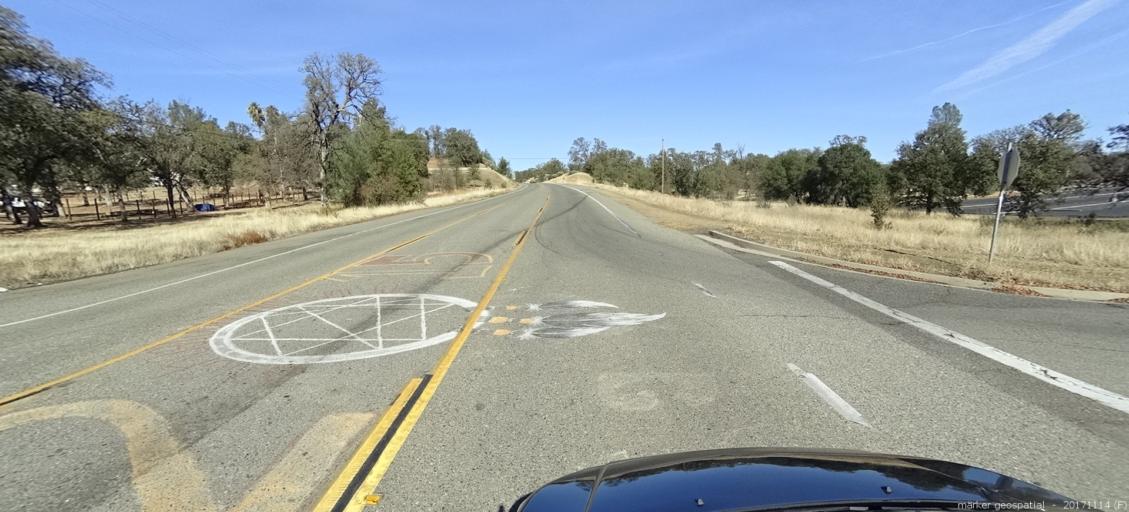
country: US
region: California
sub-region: Shasta County
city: Anderson
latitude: 40.3985
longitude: -122.4064
